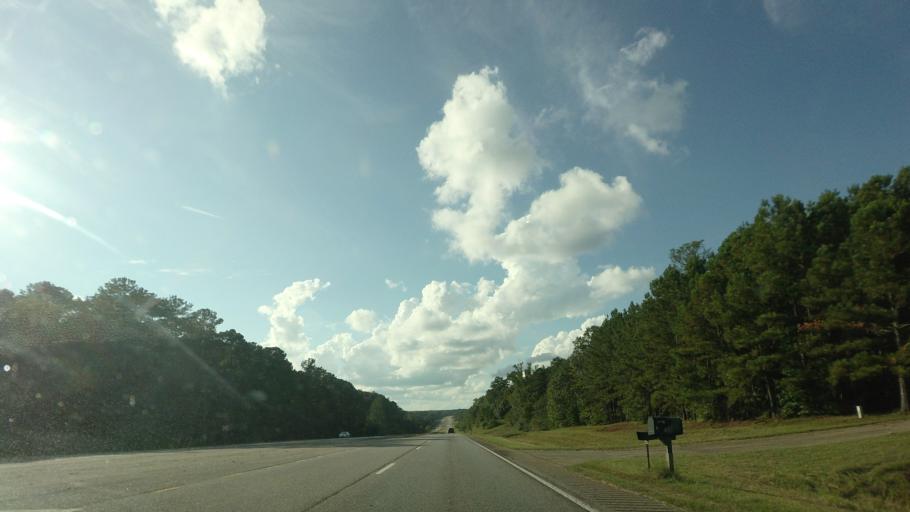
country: US
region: Georgia
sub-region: Pulaski County
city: Hawkinsville
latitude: 32.3595
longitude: -83.5961
